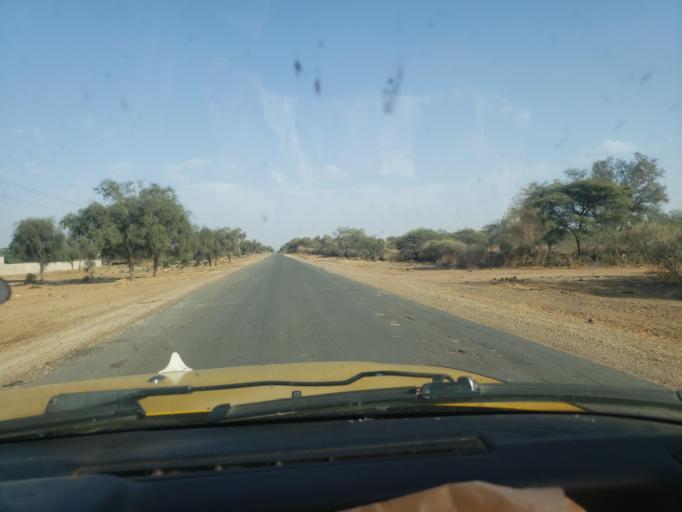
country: SN
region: Louga
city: Louga
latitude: 15.5101
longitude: -15.9816
